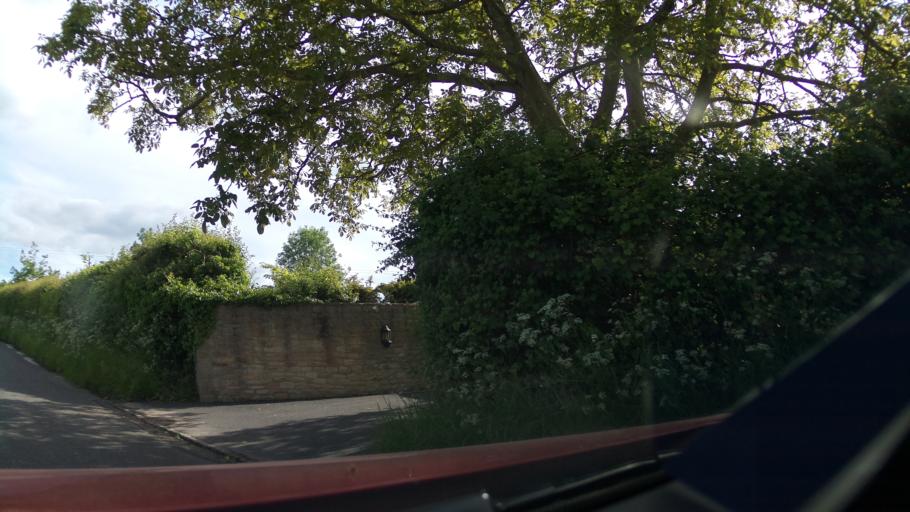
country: GB
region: England
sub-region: Gloucestershire
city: Chipping Campden
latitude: 52.0622
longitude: -1.8131
